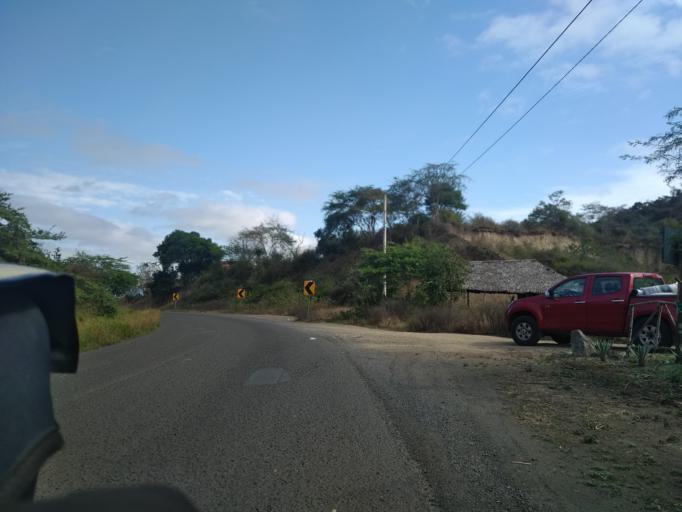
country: EC
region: Manabi
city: Jipijapa
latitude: -1.4371
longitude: -80.7563
